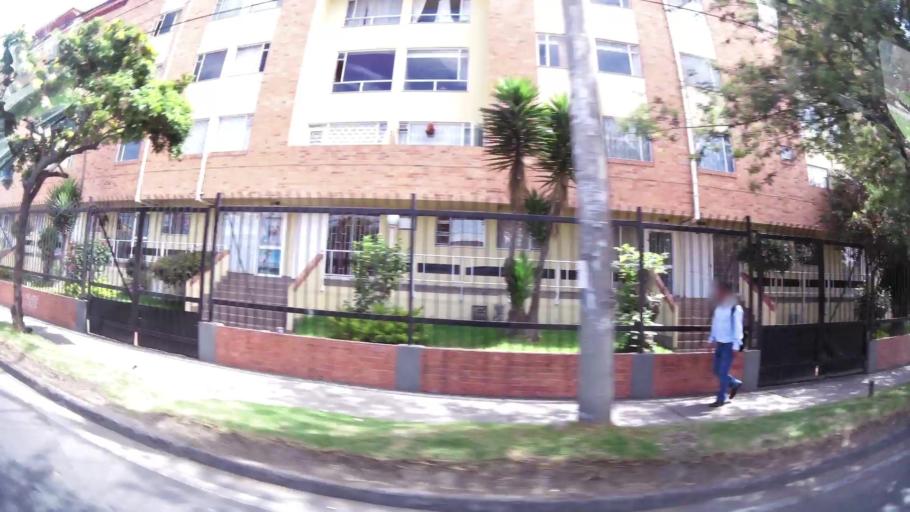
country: CO
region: Bogota D.C.
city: Bogota
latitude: 4.6253
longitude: -74.1330
